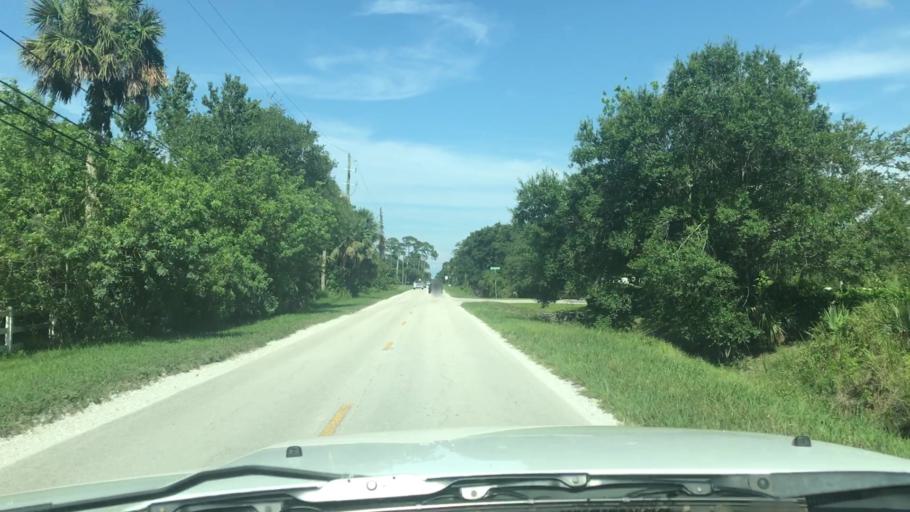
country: US
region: Florida
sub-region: Indian River County
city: West Vero Corridor
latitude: 27.6680
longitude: -80.4568
